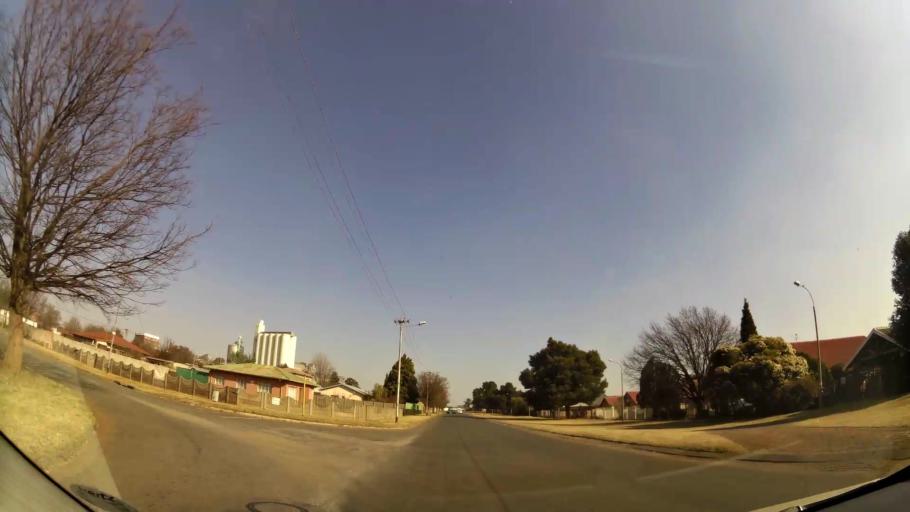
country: ZA
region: Gauteng
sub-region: West Rand District Municipality
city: Randfontein
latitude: -26.1821
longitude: 27.6922
